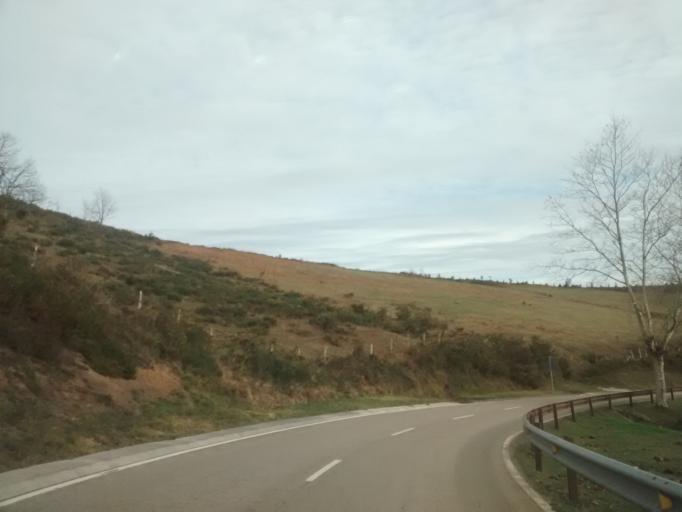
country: ES
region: Cantabria
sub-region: Provincia de Cantabria
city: Ruente
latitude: 43.2397
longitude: -4.3236
